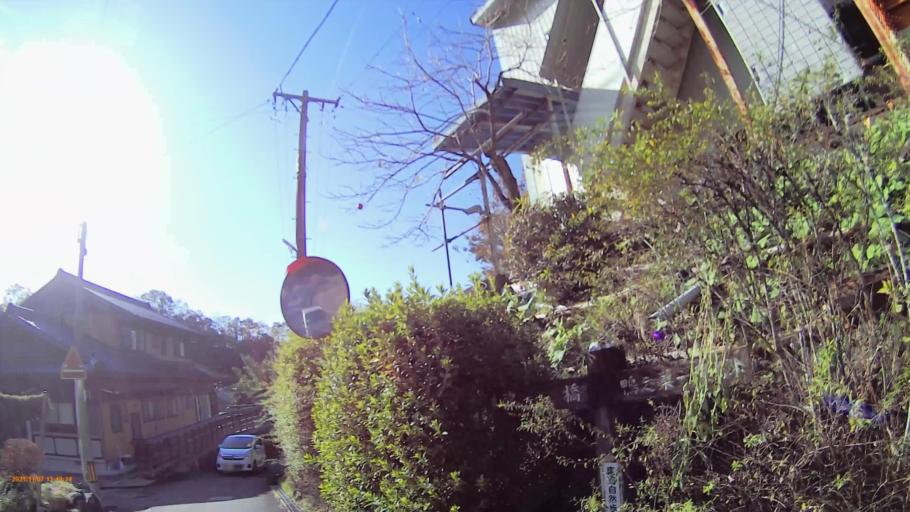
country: JP
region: Gifu
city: Mitake
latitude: 35.4265
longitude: 137.1949
